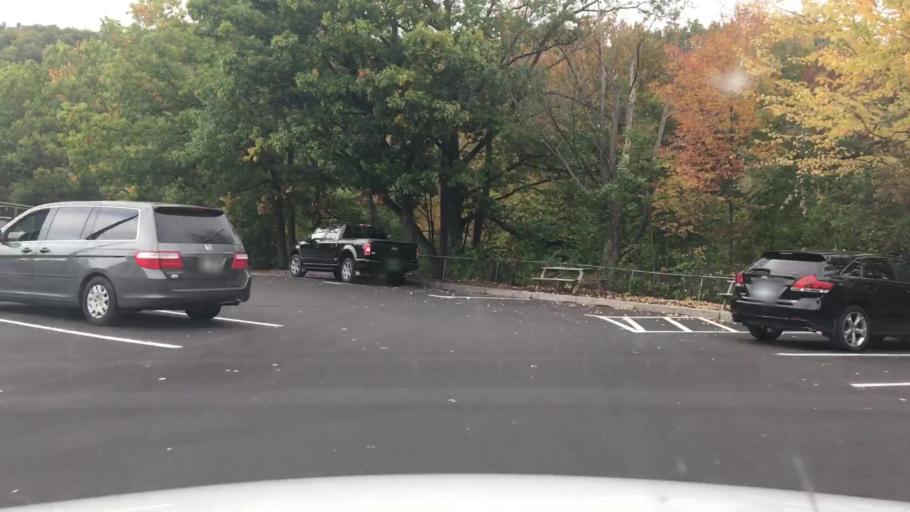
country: US
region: New Hampshire
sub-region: Coos County
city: Gorham
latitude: 44.3926
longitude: -71.1858
